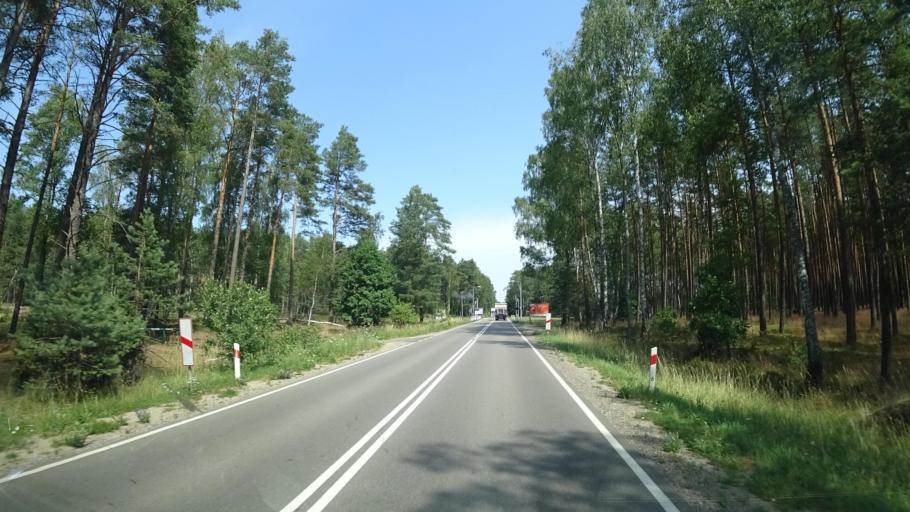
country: PL
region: Pomeranian Voivodeship
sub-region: Powiat koscierski
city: Lipusz
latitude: 54.1075
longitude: 17.8252
